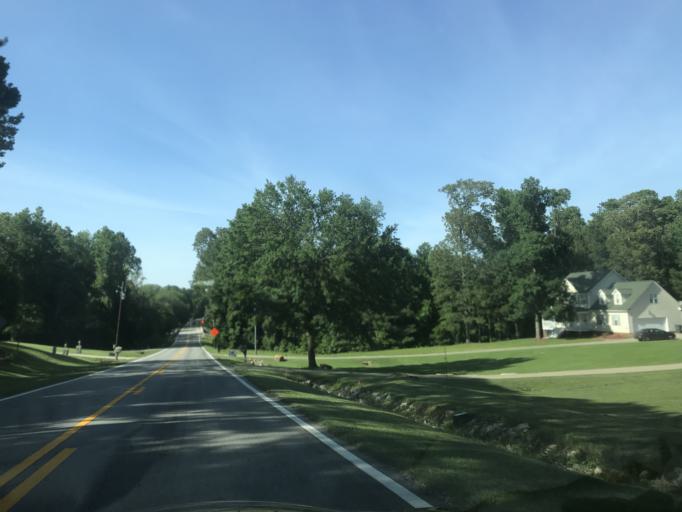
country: US
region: North Carolina
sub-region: Johnston County
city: Clayton
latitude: 35.5978
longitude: -78.5362
